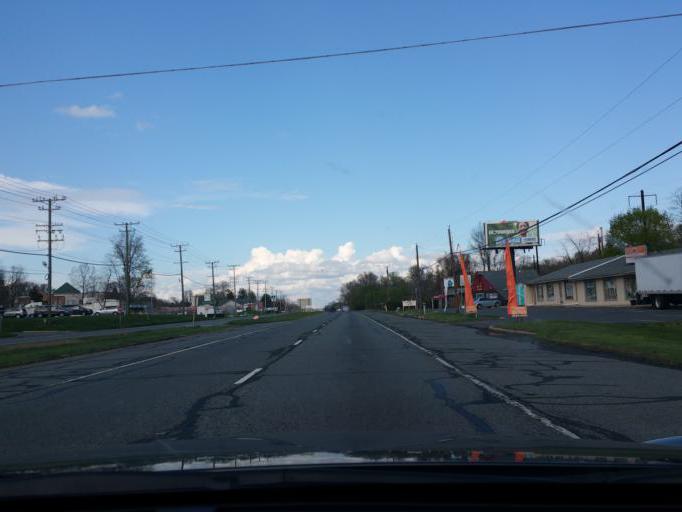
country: US
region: Maryland
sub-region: Harford County
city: Aberdeen
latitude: 39.5259
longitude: -76.1348
